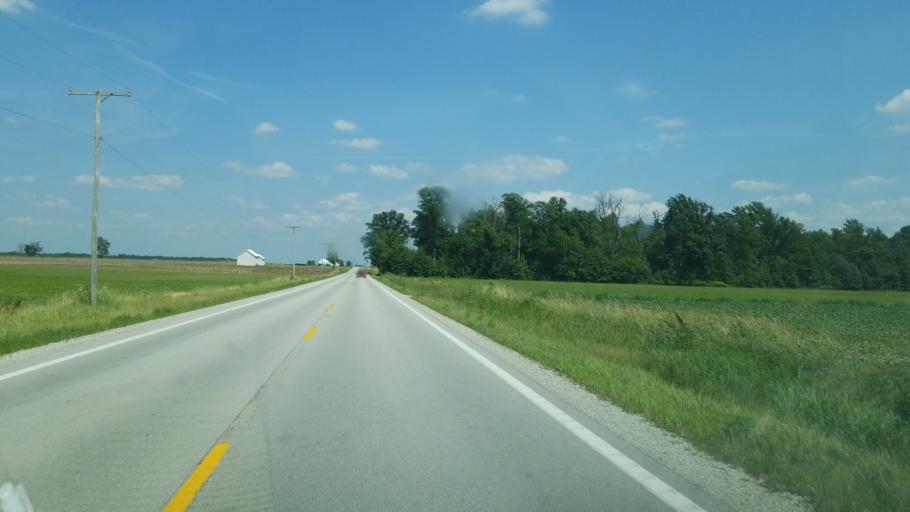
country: US
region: Ohio
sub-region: Huron County
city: Bellevue
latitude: 41.1245
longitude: -82.8781
